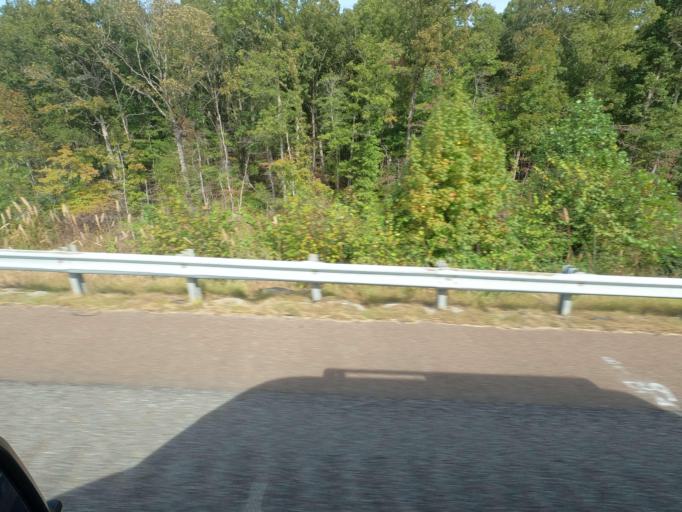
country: US
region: Tennessee
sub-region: Humphreys County
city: New Johnsonville
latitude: 35.8705
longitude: -88.0137
